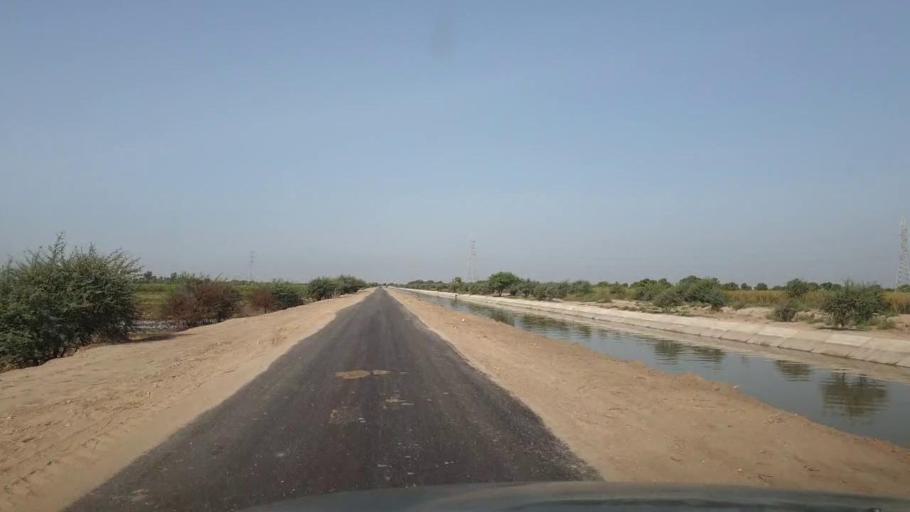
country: PK
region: Sindh
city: Tando Muhammad Khan
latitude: 25.1131
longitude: 68.3999
